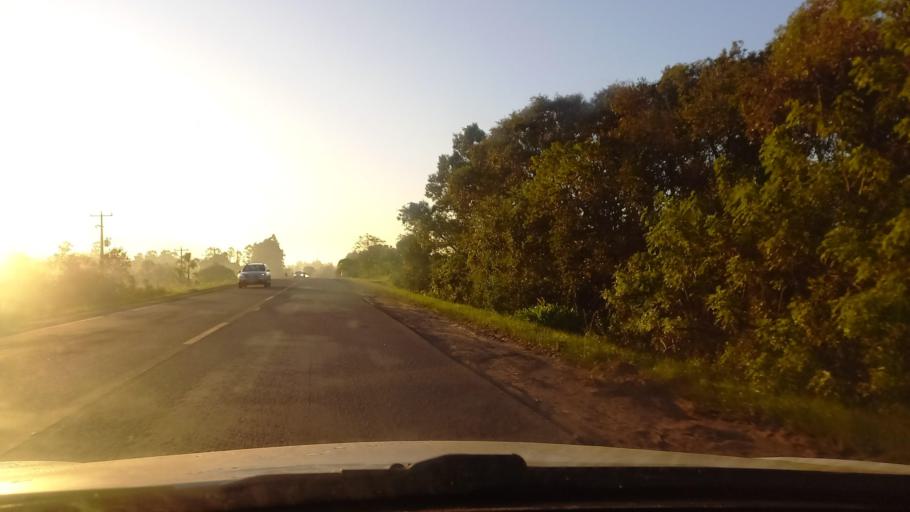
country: BR
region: Rio Grande do Sul
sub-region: Candelaria
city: Candelaria
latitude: -29.6807
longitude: -52.8296
